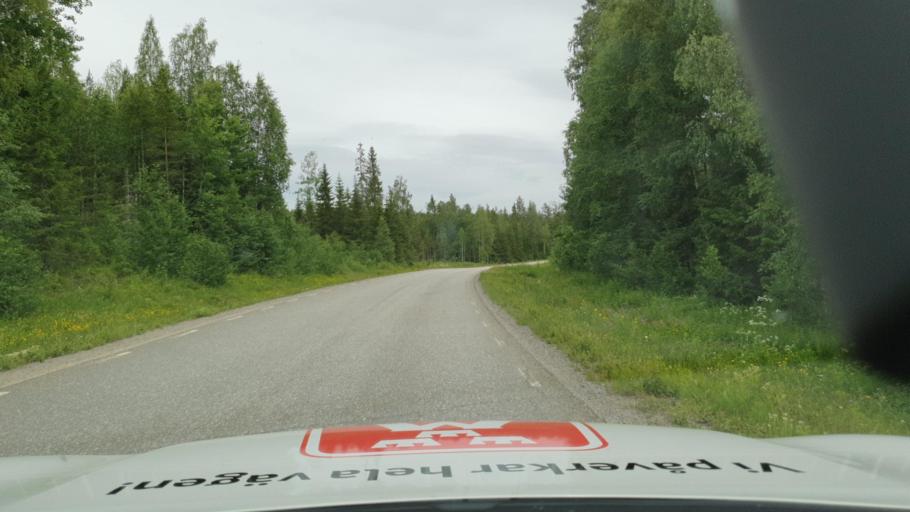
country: SE
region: Vaesterbotten
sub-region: Skelleftea Kommun
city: Burtraesk
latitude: 64.2937
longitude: 20.6460
